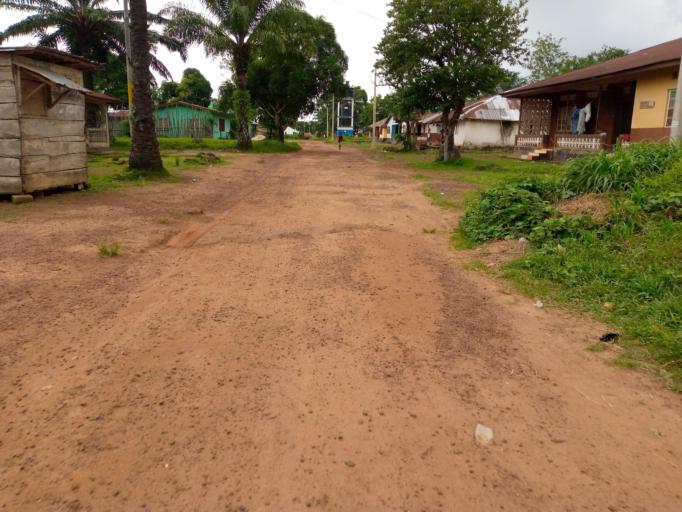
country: SL
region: Southern Province
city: Moyamba
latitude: 8.1515
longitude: -12.4355
